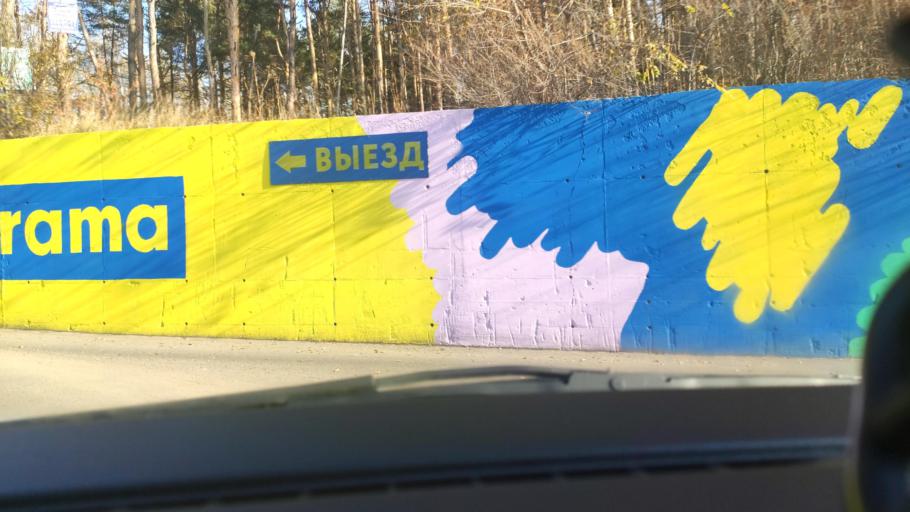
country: RU
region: Voronezj
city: Pridonskoy
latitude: 51.6462
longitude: 39.1146
